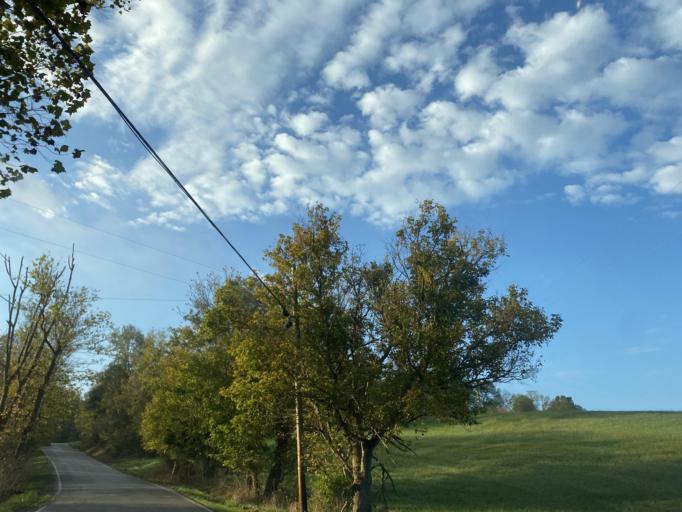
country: US
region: Kentucky
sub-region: Pendleton County
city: Falmouth
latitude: 38.7706
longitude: -84.3385
